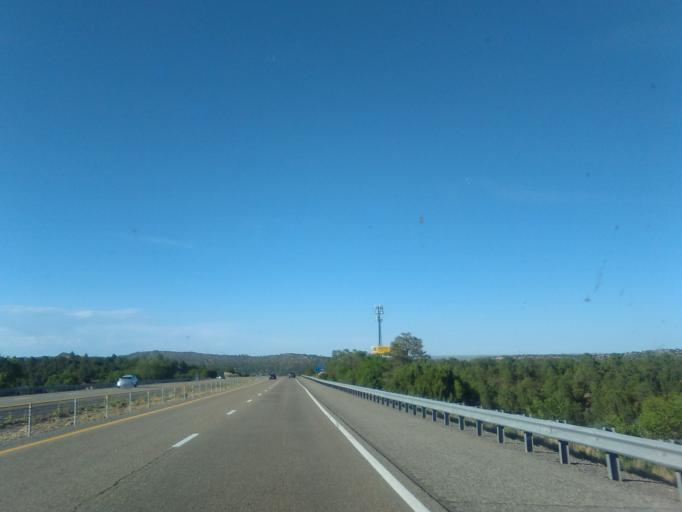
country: US
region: New Mexico
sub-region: San Miguel County
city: Las Vegas
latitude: 35.5093
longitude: -105.2576
